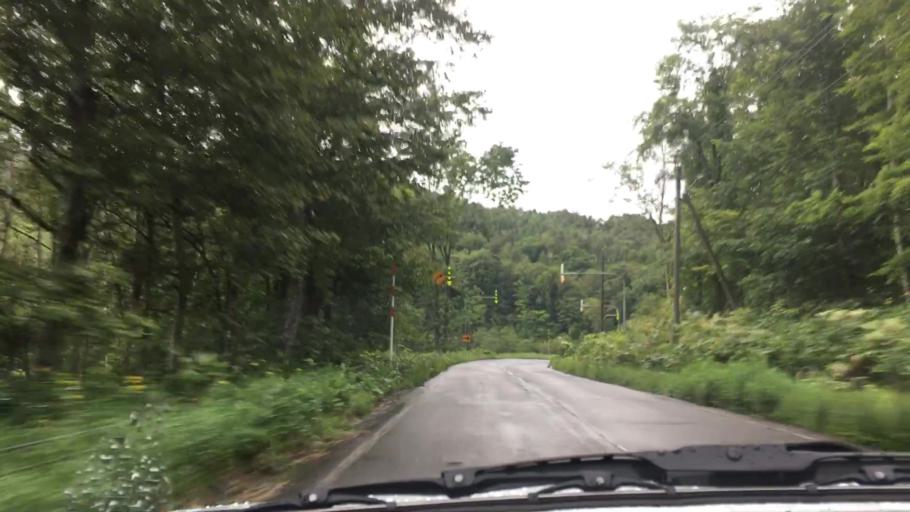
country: JP
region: Hokkaido
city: Niseko Town
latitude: 42.6641
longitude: 140.7772
